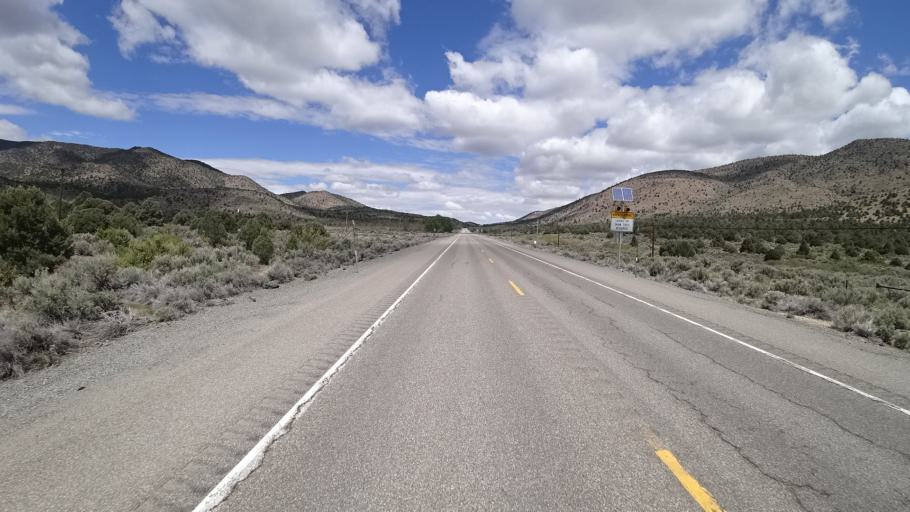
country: US
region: Nevada
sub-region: Lyon County
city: Smith Valley
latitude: 38.7451
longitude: -119.5656
